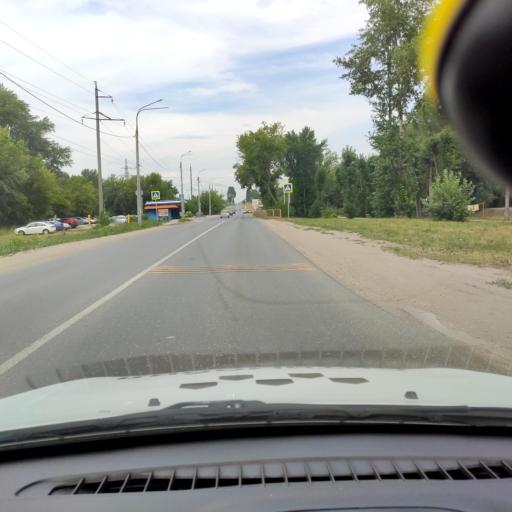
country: RU
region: Samara
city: Zhigulevsk
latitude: 53.4076
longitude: 49.5237
